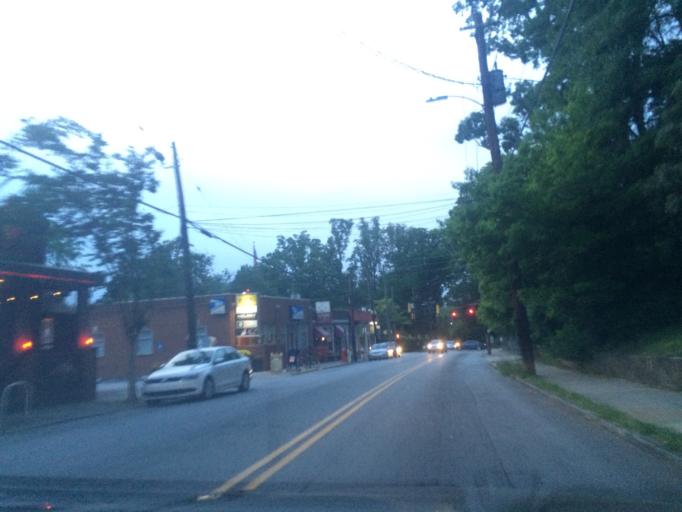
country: US
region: Georgia
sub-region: DeKalb County
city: Druid Hills
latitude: 33.7868
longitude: -84.3553
